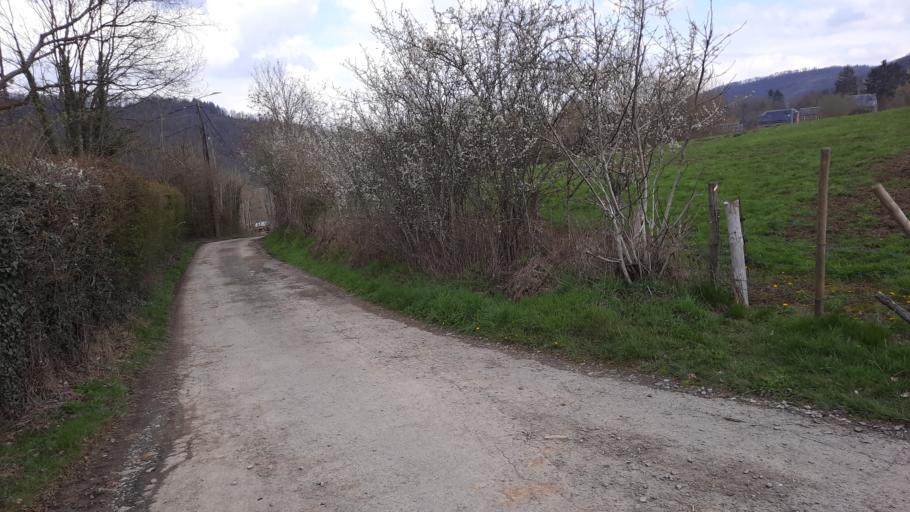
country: BE
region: Wallonia
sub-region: Province du Luxembourg
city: Rendeux
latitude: 50.2132
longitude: 5.5263
